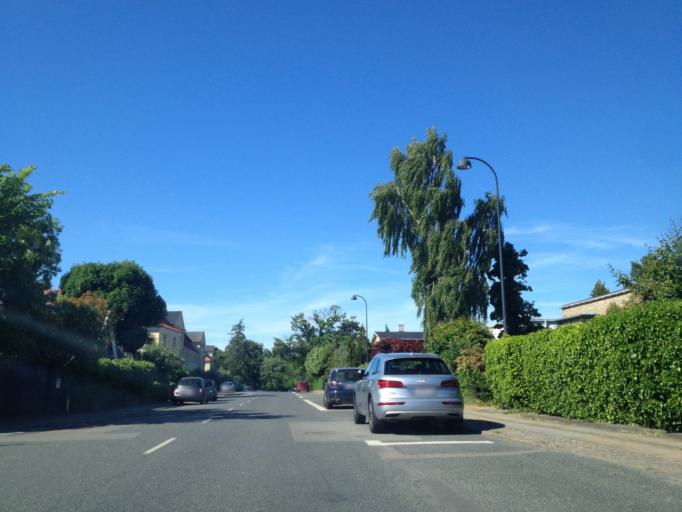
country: DK
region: Capital Region
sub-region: Gentofte Kommune
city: Charlottenlund
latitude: 55.7654
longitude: 12.5865
